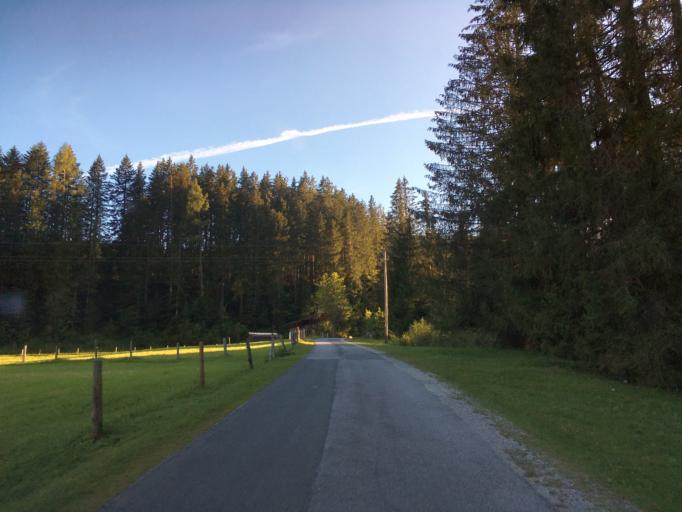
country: AT
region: Salzburg
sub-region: Politischer Bezirk Hallein
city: Abtenau
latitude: 47.4982
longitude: 13.3763
